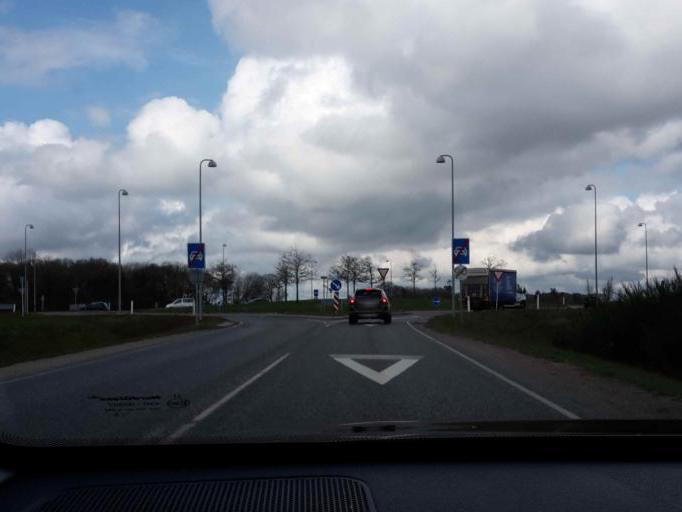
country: DK
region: South Denmark
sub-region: Billund Kommune
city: Billund
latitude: 55.7486
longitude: 9.1401
